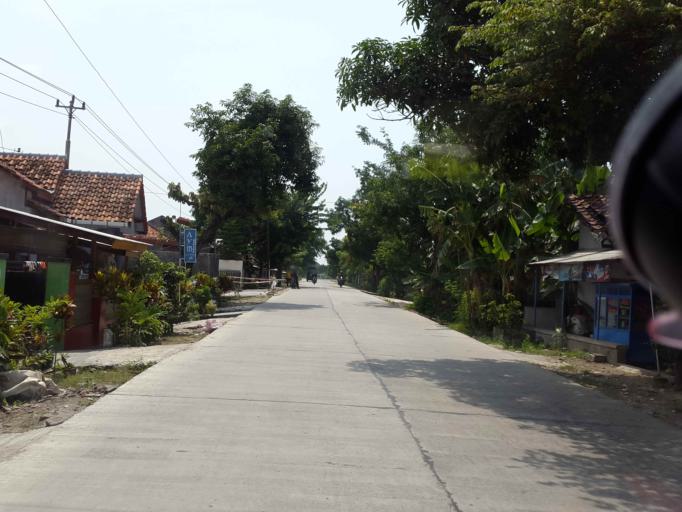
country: ID
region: Central Java
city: Pemalang
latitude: -6.9076
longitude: 109.3989
